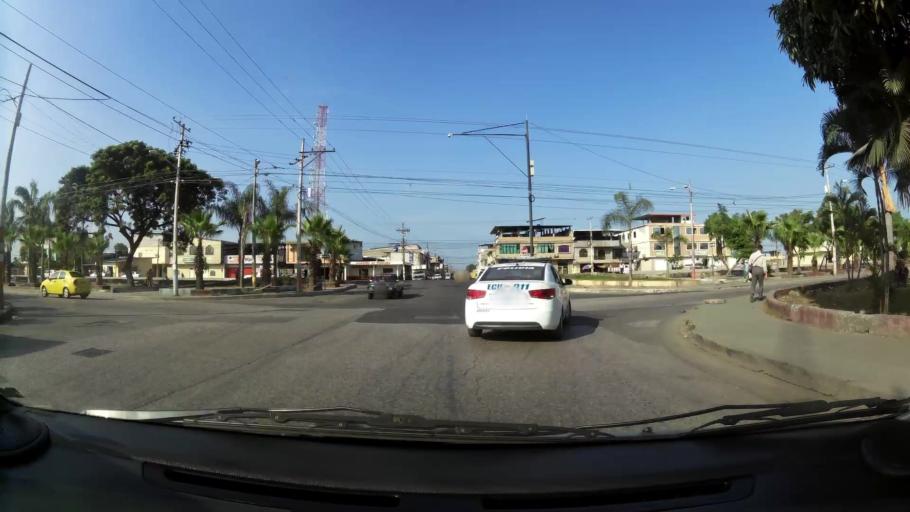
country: EC
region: Guayas
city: Eloy Alfaro
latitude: -2.1798
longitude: -79.8449
